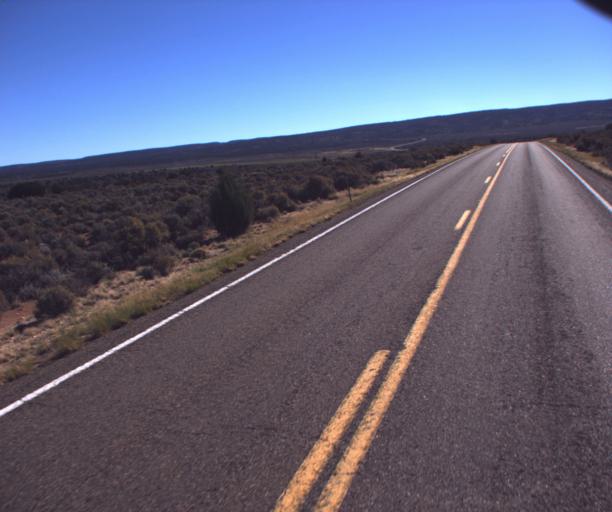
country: US
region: Arizona
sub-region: Coconino County
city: Fredonia
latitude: 36.8608
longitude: -112.3110
